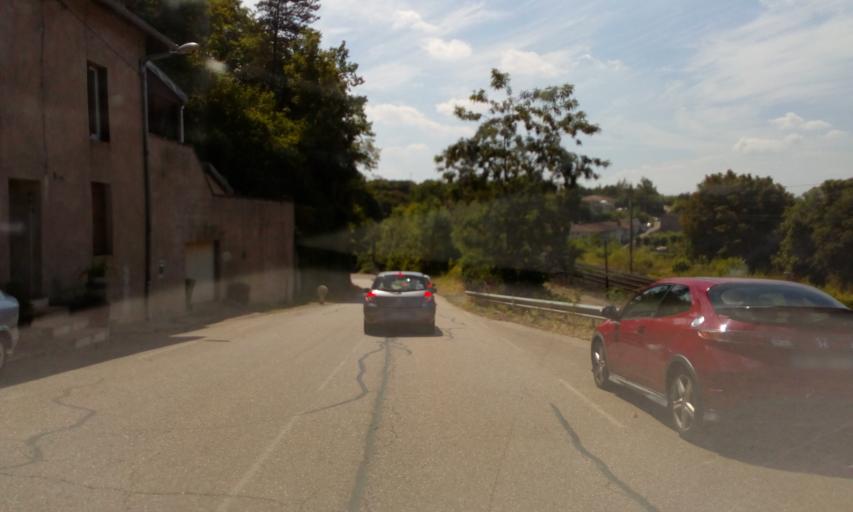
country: FR
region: Lorraine
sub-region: Departement de Meurthe-et-Moselle
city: Pagny-sur-Moselle
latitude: 48.9531
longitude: 5.8691
